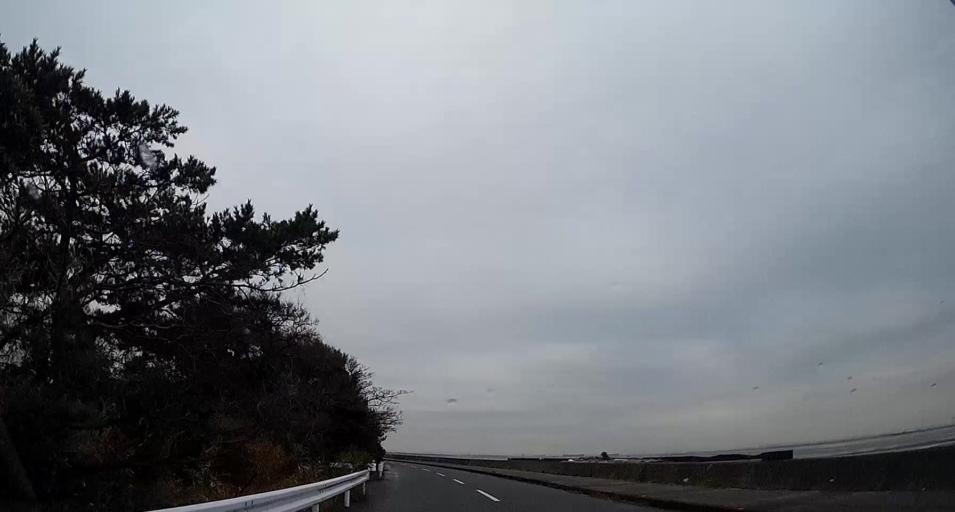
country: JP
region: Chiba
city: Kisarazu
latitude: 35.4366
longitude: 139.9149
